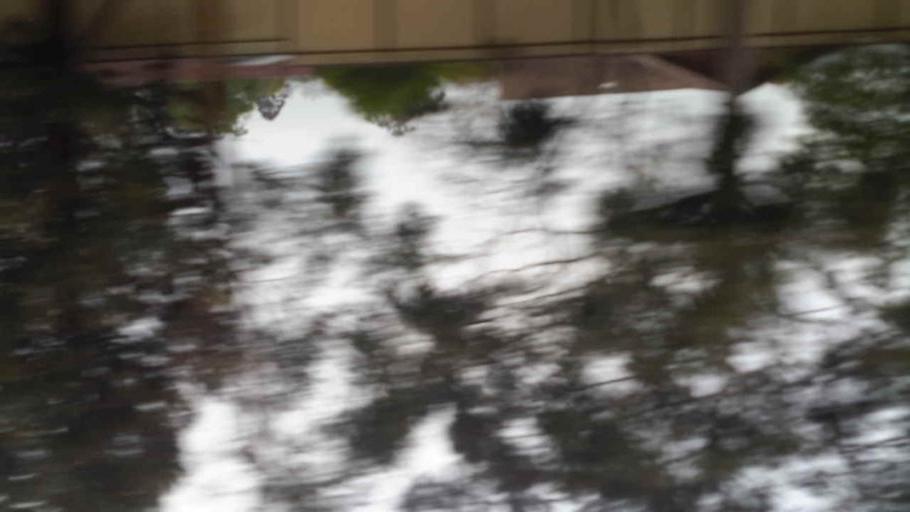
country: AU
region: New South Wales
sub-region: Camden
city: Camden South
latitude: -34.0880
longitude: 150.6950
